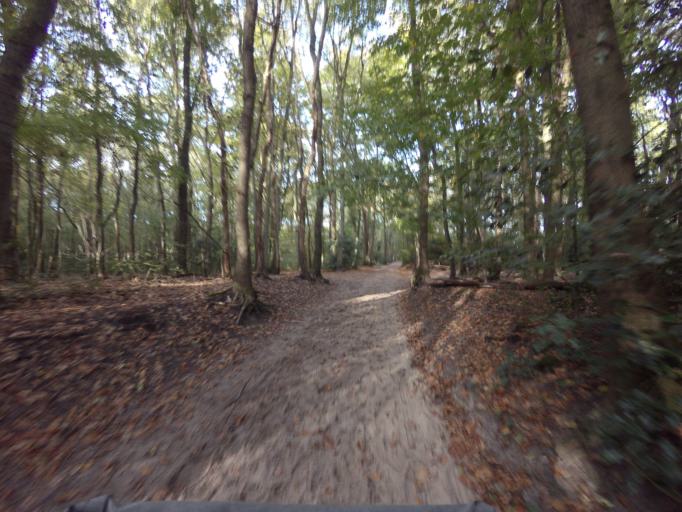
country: NL
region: North Holland
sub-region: Gemeente Blaricum
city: Blaricum
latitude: 52.2824
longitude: 5.2357
